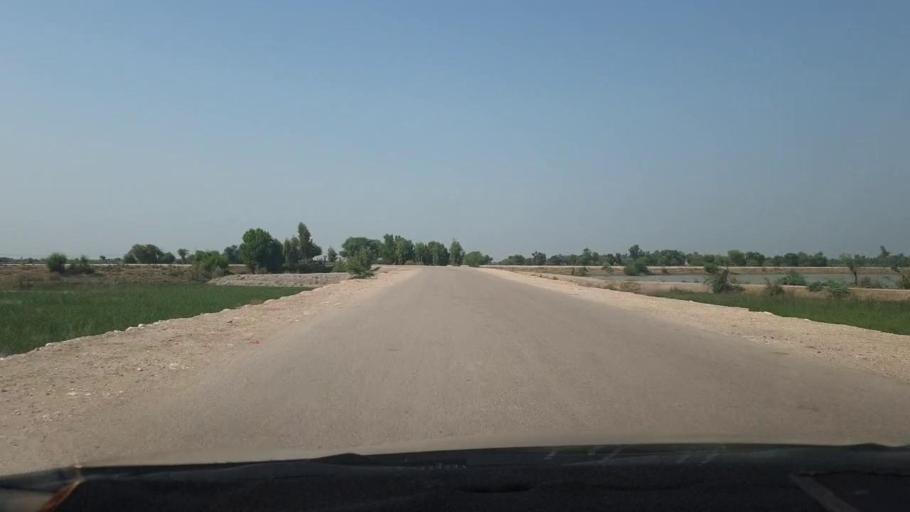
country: PK
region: Sindh
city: Larkana
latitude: 27.5966
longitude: 68.2436
